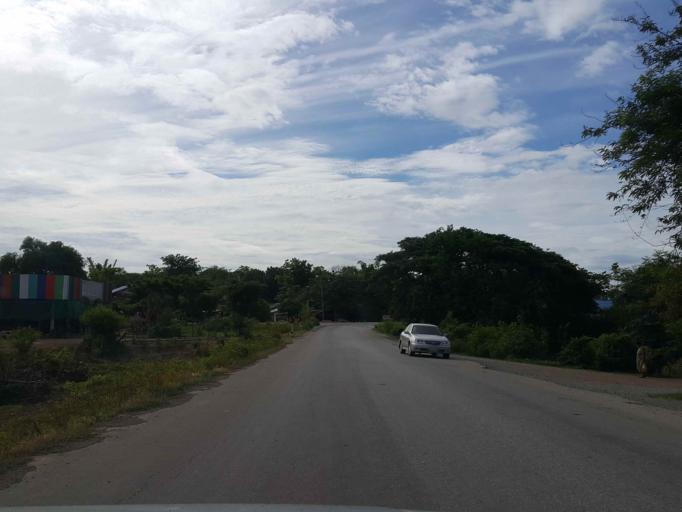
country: TH
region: Sukhothai
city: Thung Saliam
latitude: 17.2701
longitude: 99.5333
